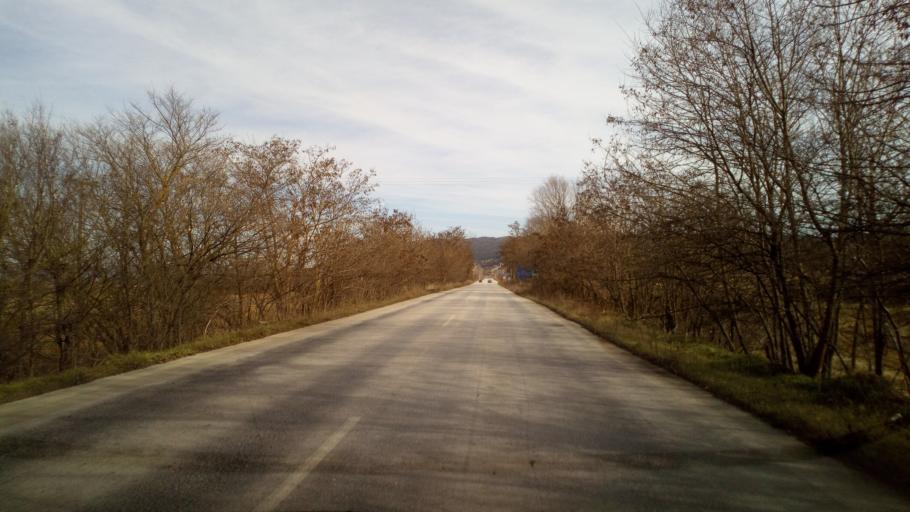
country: GR
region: Central Macedonia
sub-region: Nomos Thessalonikis
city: Gerakarou
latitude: 40.6329
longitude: 23.2338
